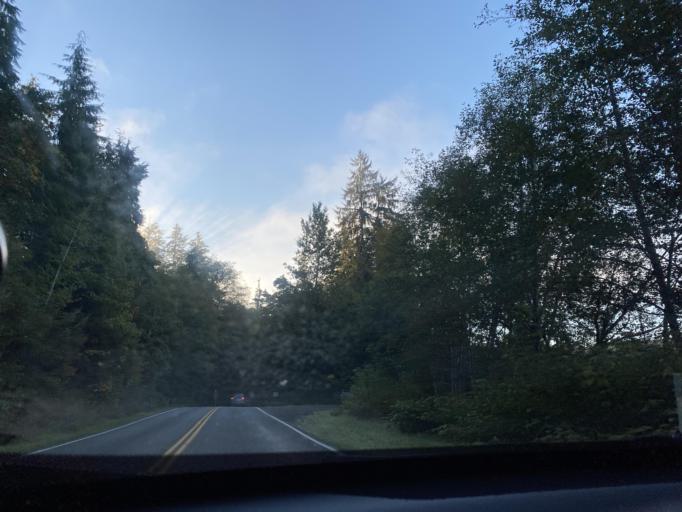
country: US
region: Washington
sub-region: Clallam County
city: Forks
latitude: 47.8196
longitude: -124.1765
